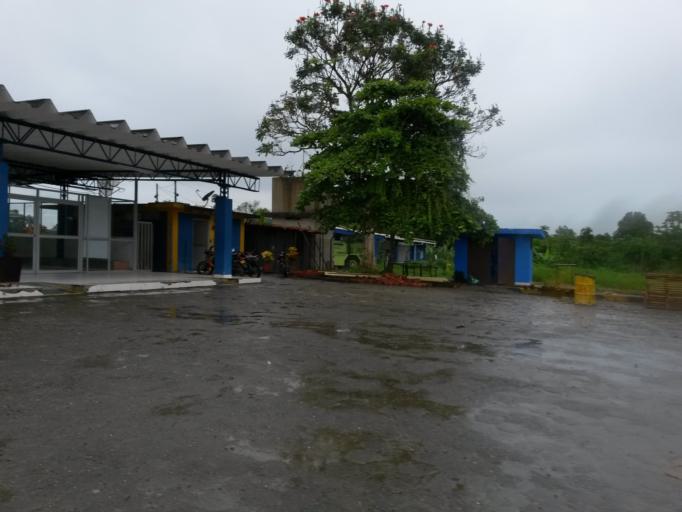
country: CO
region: Cauca
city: Guapi
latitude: 2.5751
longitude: -77.8945
